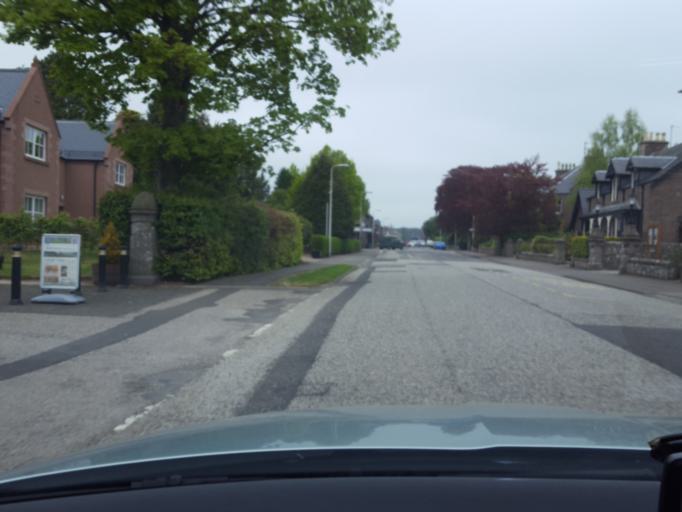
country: GB
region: Scotland
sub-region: Angus
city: Brechin
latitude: 56.8070
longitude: -2.6541
